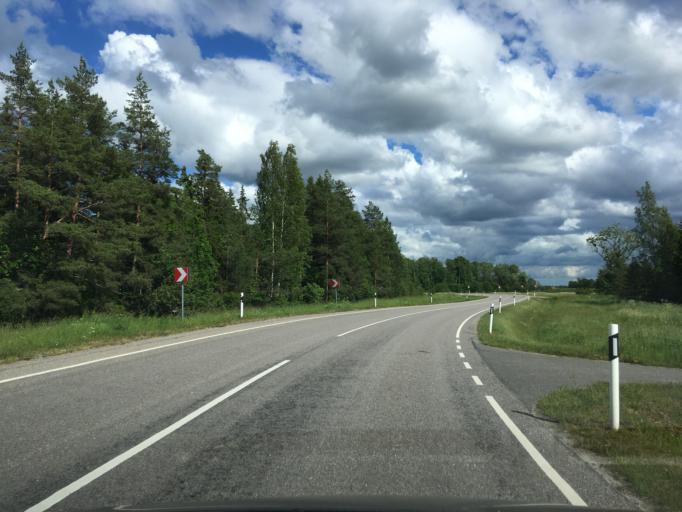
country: EE
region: Paernumaa
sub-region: Halinga vald
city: Parnu-Jaagupi
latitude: 58.6749
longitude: 24.6126
